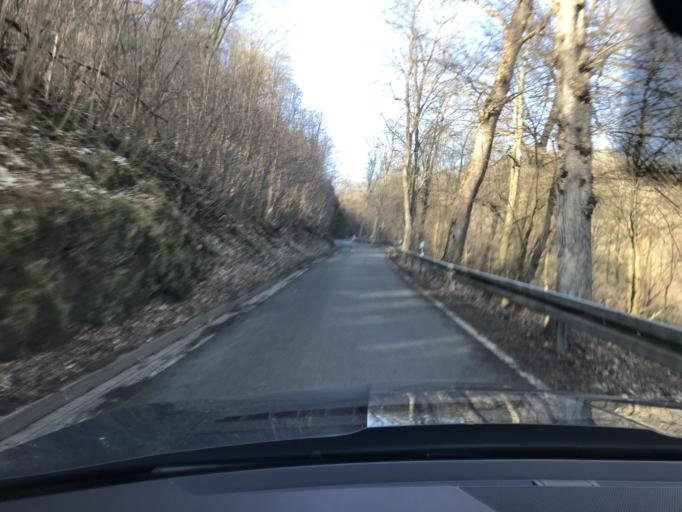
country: DE
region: Saxony-Anhalt
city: Timmenrode
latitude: 51.7207
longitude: 10.9691
